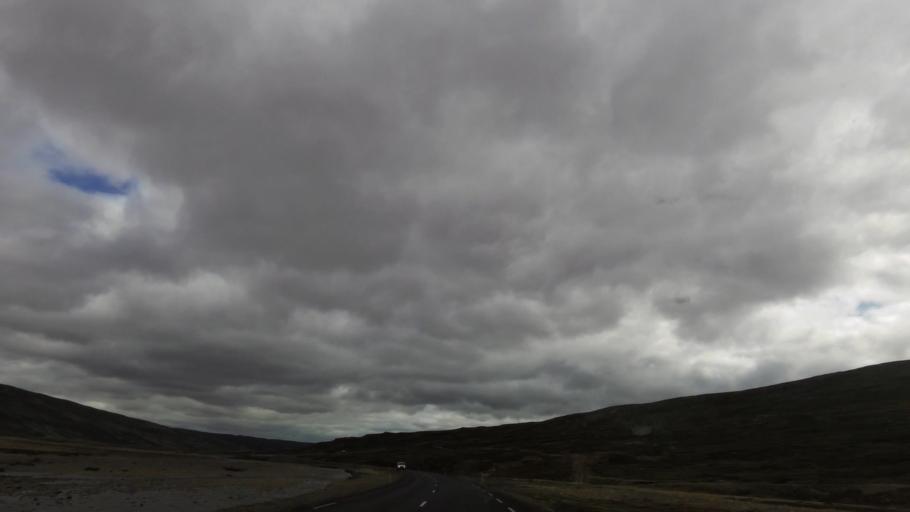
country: IS
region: West
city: Stykkisholmur
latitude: 65.7580
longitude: -21.8664
